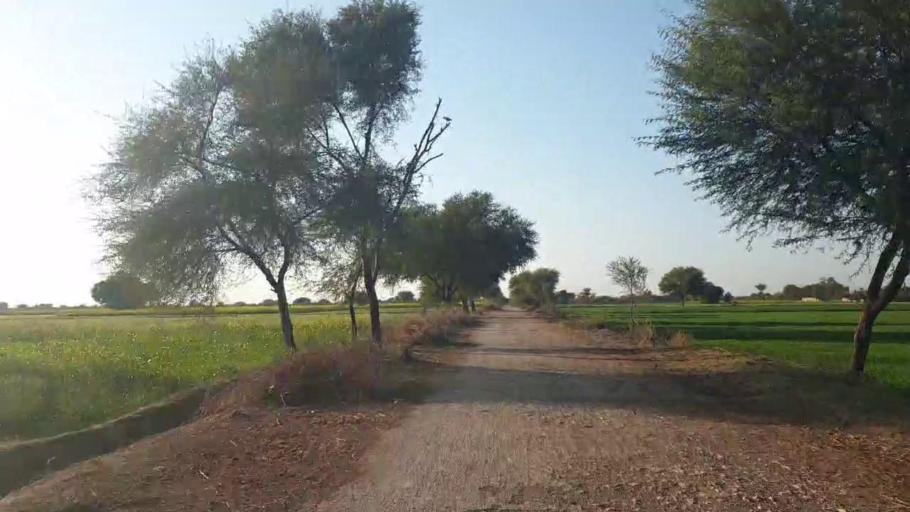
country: PK
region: Sindh
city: Shahpur Chakar
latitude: 26.0615
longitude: 68.6543
